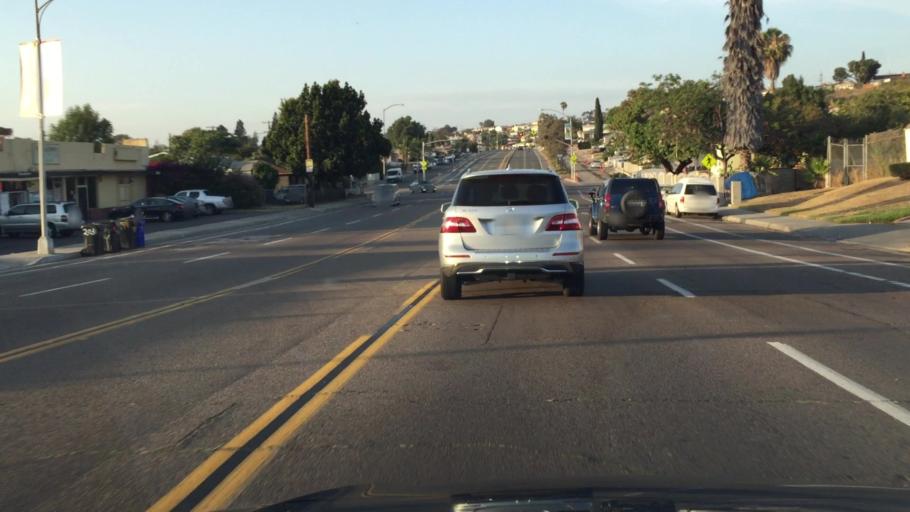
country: US
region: California
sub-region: San Diego County
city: National City
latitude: 32.7251
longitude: -117.0838
